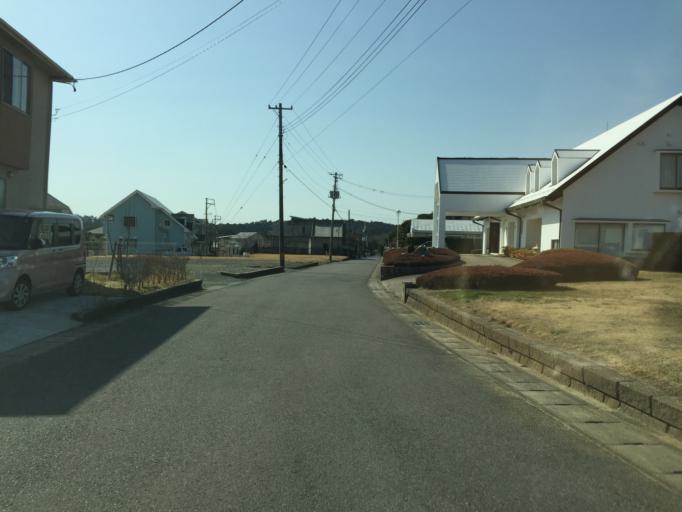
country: JP
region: Fukushima
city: Iwaki
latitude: 36.9686
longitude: 140.9380
